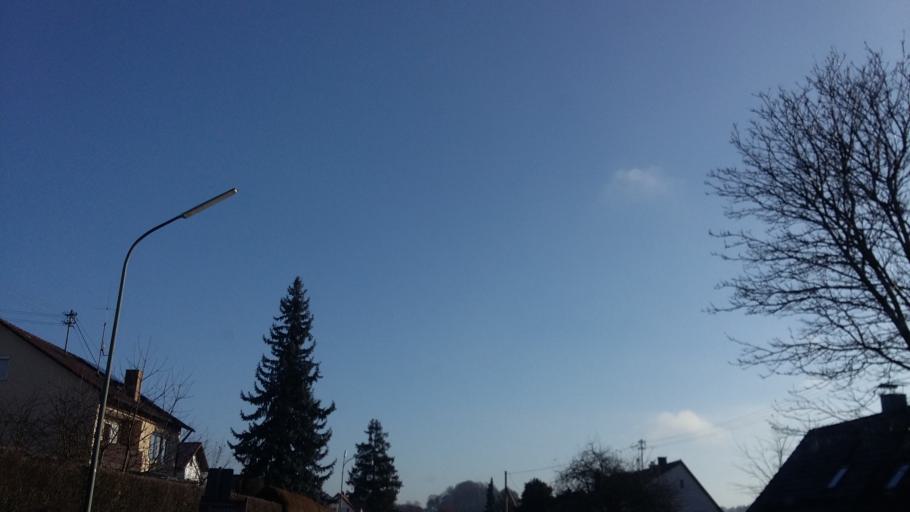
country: DE
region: Bavaria
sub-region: Swabia
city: Adelzhausen
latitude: 48.3593
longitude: 11.1392
